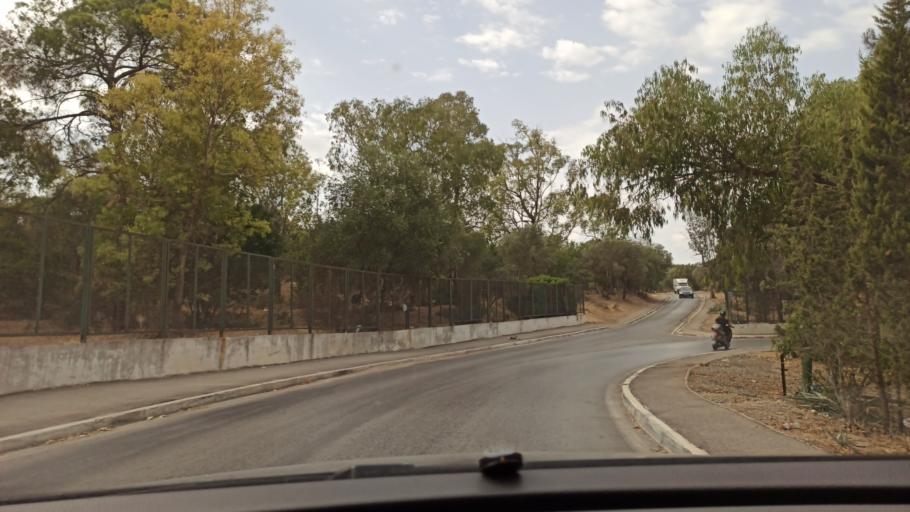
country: TN
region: Tunis
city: Tunis
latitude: 36.8250
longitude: 10.1691
